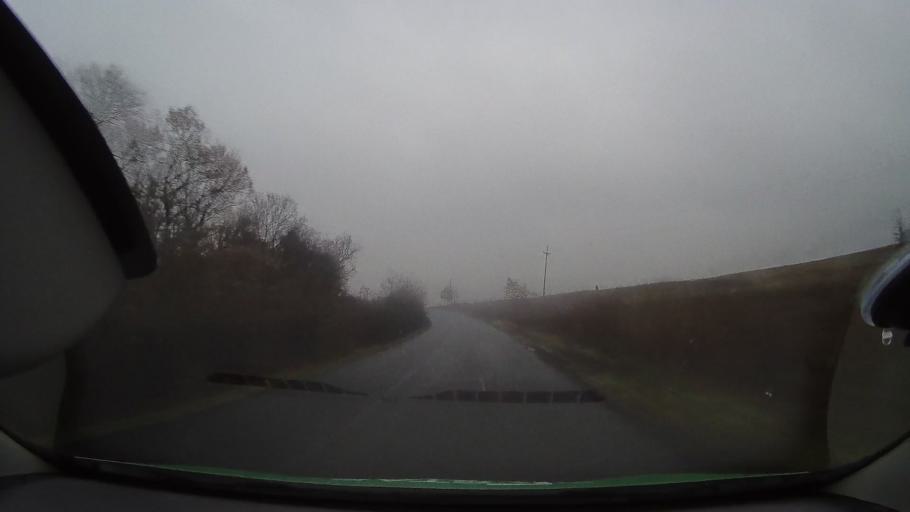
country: RO
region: Bihor
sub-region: Comuna Tinca
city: Gurbediu
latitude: 46.7756
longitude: 21.8811
